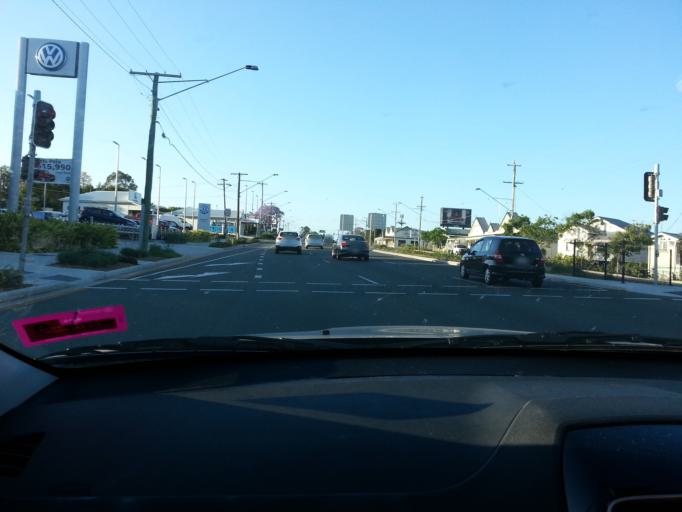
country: AU
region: Queensland
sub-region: Brisbane
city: Gordon Park
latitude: -27.4070
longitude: 153.0324
